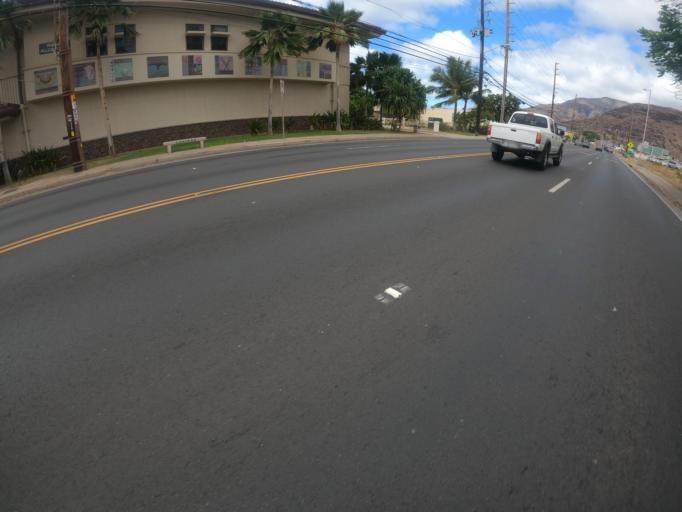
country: US
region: Hawaii
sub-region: Honolulu County
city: Waianae
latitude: 21.4436
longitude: -158.1873
